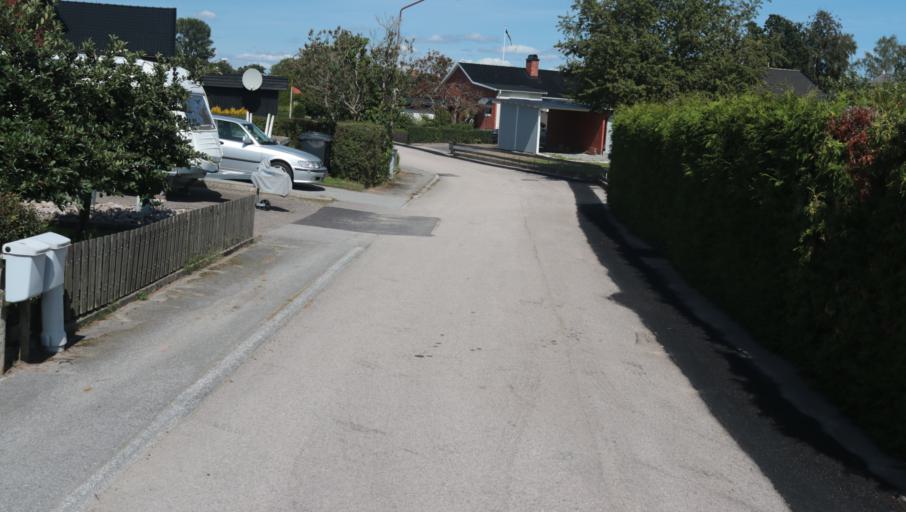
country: SE
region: Blekinge
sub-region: Karlshamns Kommun
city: Karlshamn
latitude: 56.1999
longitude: 14.8234
